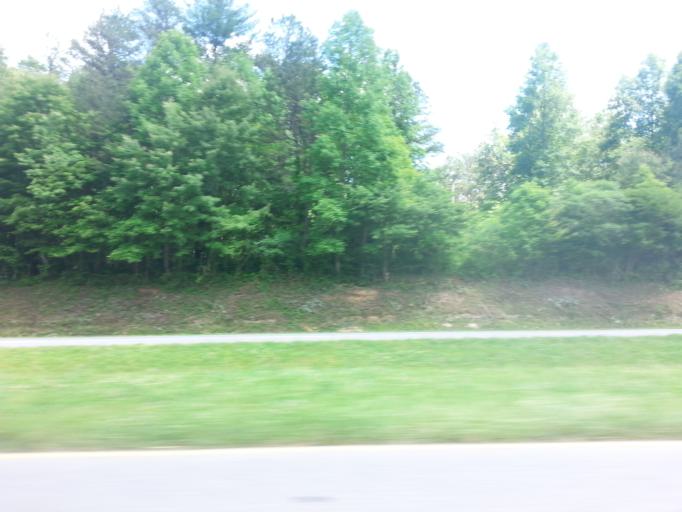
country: US
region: North Carolina
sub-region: Cherokee County
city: Murphy
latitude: 35.0474
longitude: -84.0780
